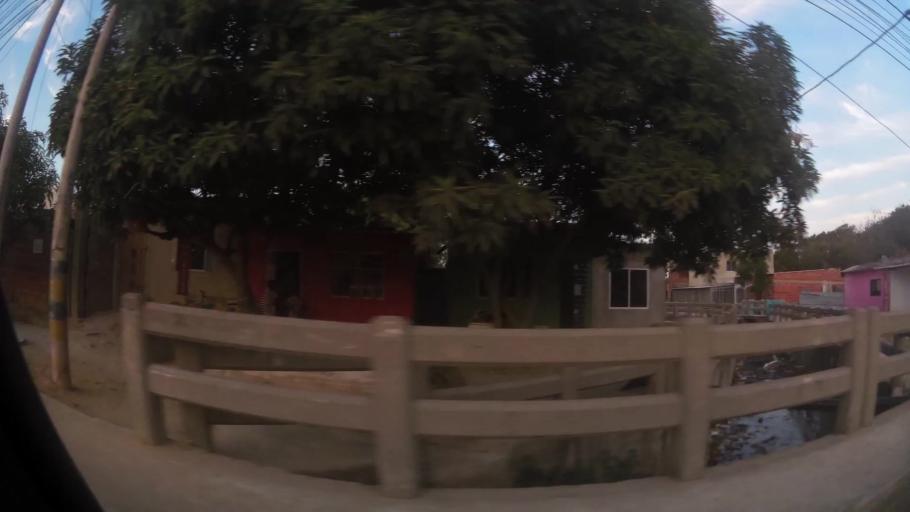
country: CO
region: Atlantico
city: Barranquilla
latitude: 10.9611
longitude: -74.8271
